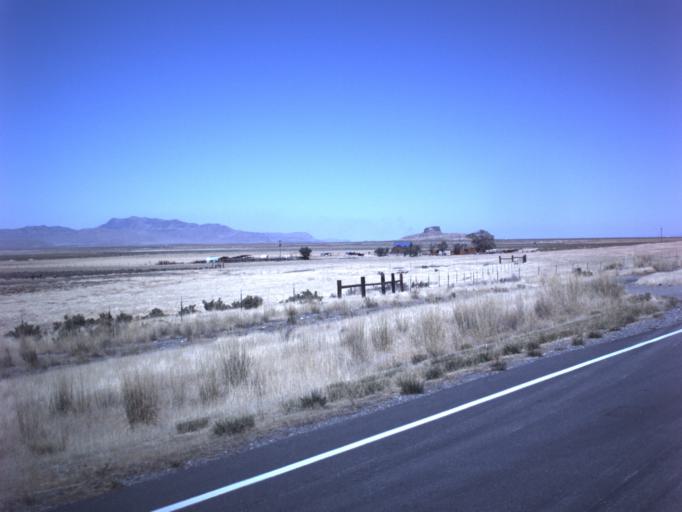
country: US
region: Utah
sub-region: Tooele County
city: Grantsville
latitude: 40.6668
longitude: -112.6756
